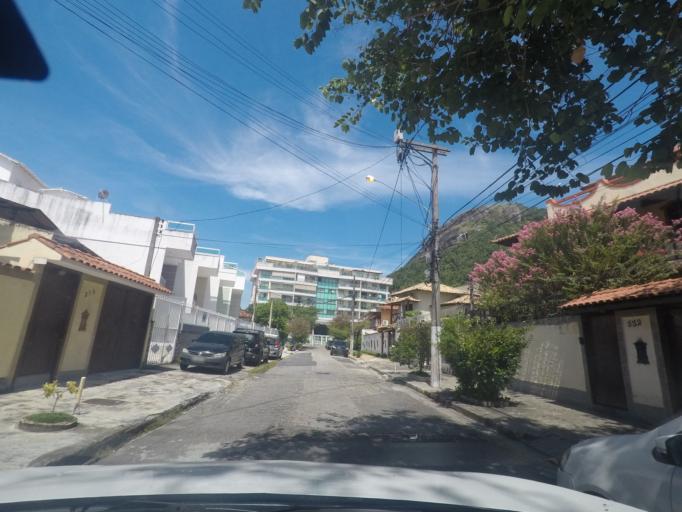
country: BR
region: Rio de Janeiro
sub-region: Niteroi
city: Niteroi
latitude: -22.9153
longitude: -43.0846
